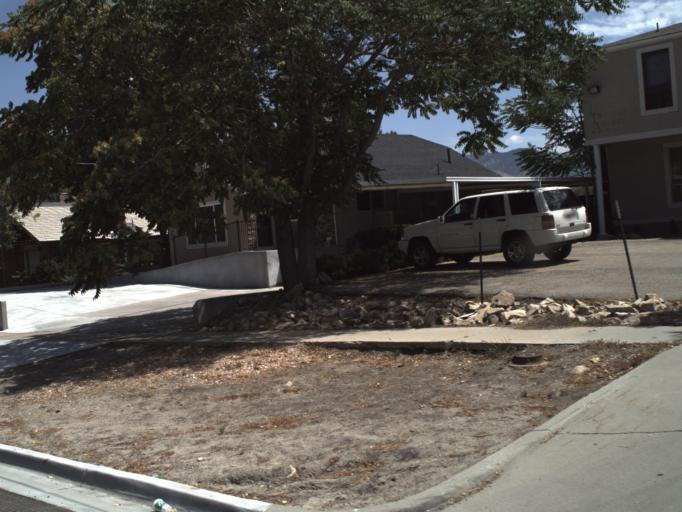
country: US
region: Utah
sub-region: Tooele County
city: Tooele
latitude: 40.5344
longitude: -112.2984
